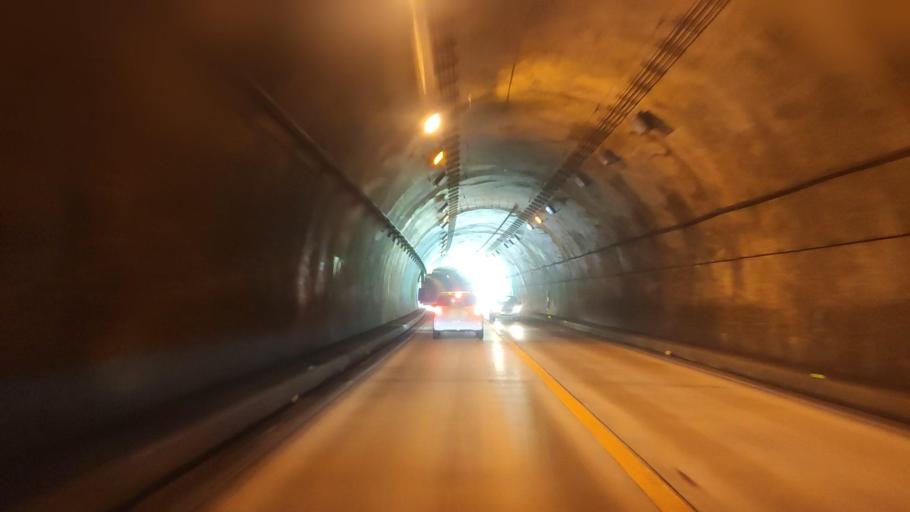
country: JP
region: Nara
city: Yoshino-cho
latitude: 34.2603
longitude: 136.0024
